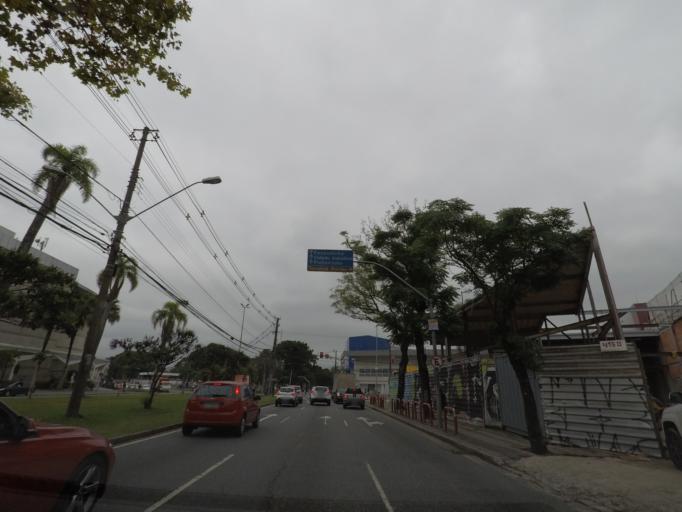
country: BR
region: Parana
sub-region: Curitiba
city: Curitiba
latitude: -25.4772
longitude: -49.2917
